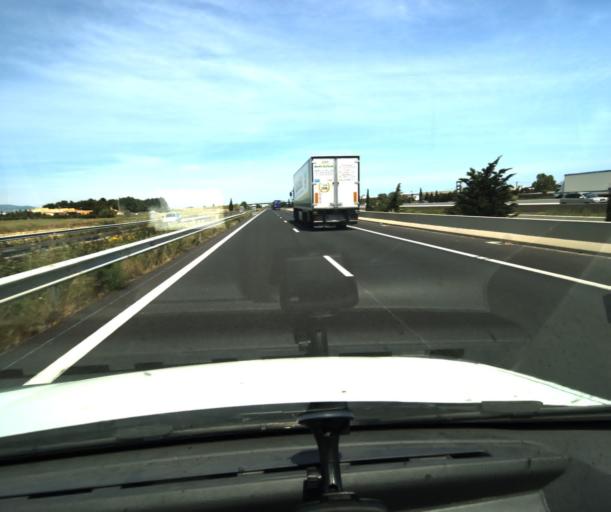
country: FR
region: Languedoc-Roussillon
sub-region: Departement des Pyrenees-Orientales
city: Rivesaltes
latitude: 42.7357
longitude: 2.8841
